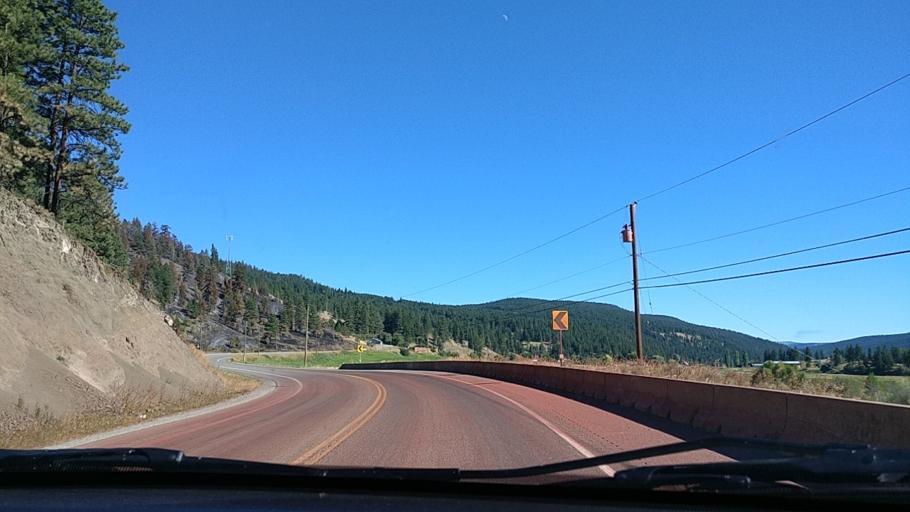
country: CA
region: British Columbia
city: Chase
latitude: 50.5338
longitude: -119.8410
